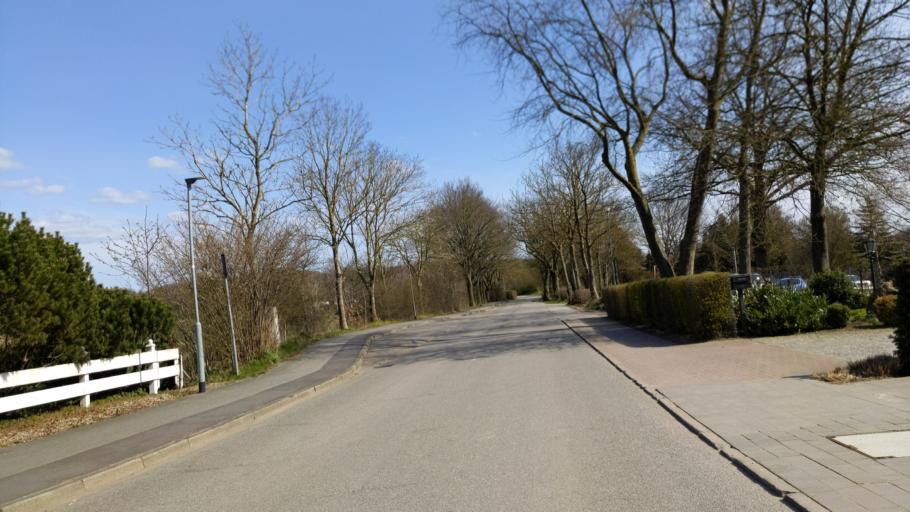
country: DE
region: Schleswig-Holstein
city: Schashagen
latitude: 54.1291
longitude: 10.8606
